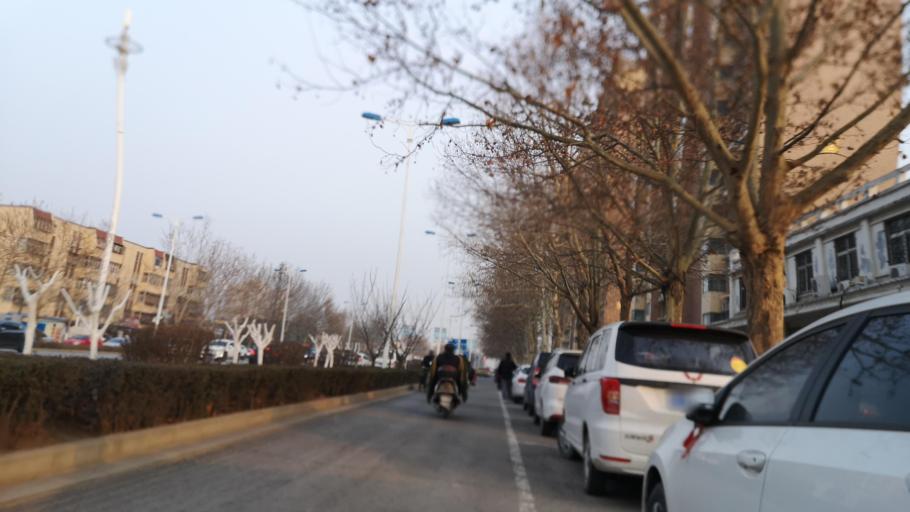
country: CN
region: Henan Sheng
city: Zhongyuanlu
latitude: 35.7649
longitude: 115.0952
